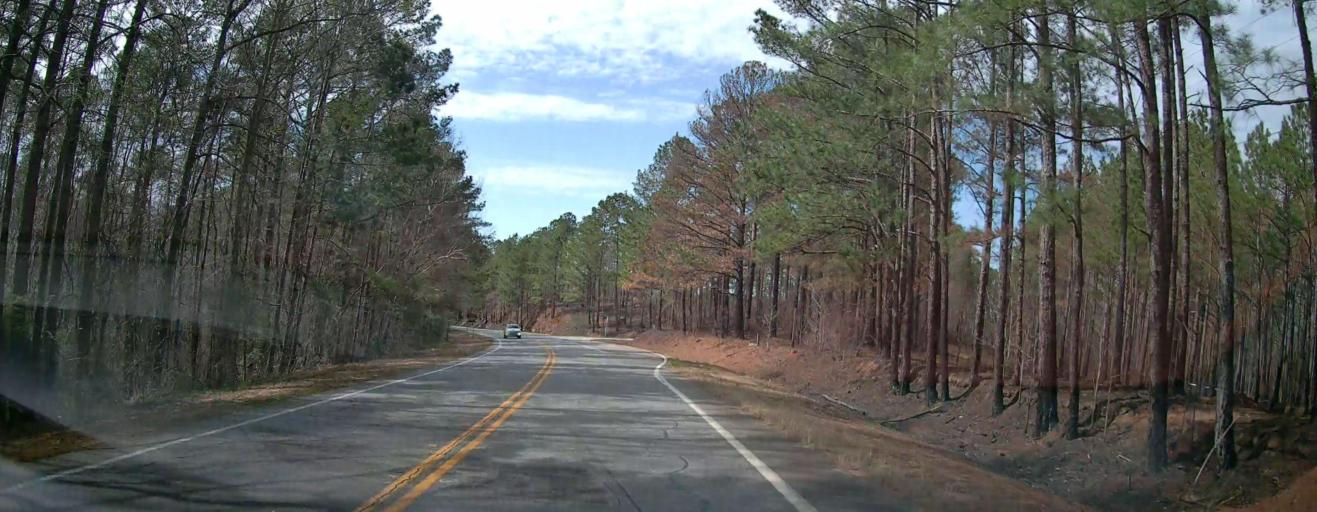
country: US
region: Georgia
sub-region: Jones County
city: Gray
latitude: 33.0159
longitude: -83.7042
